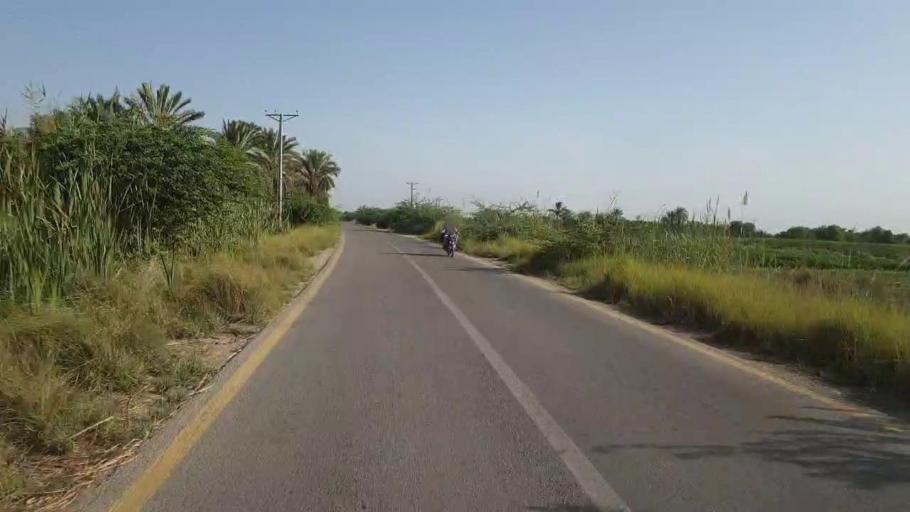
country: PK
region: Sindh
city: Daur
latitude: 26.4597
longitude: 68.4507
